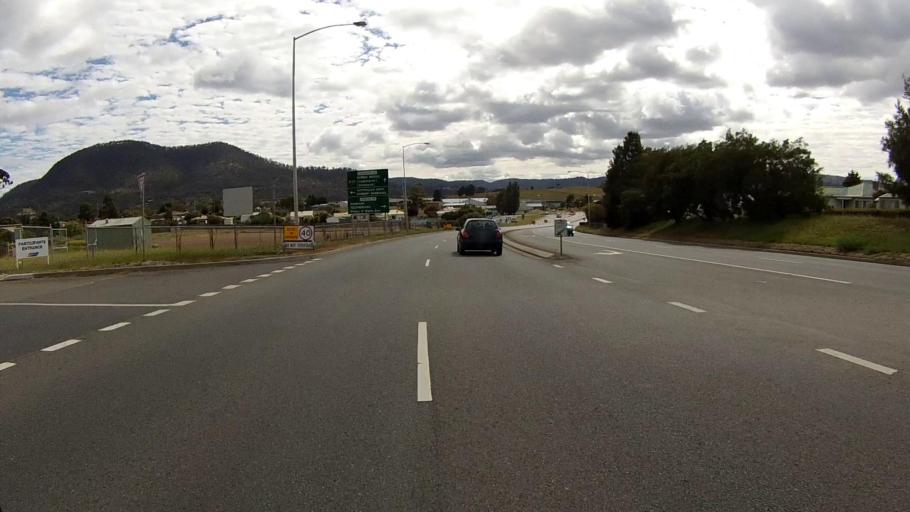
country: AU
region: Tasmania
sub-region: Glenorchy
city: Goodwood
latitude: -42.8242
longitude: 147.2915
